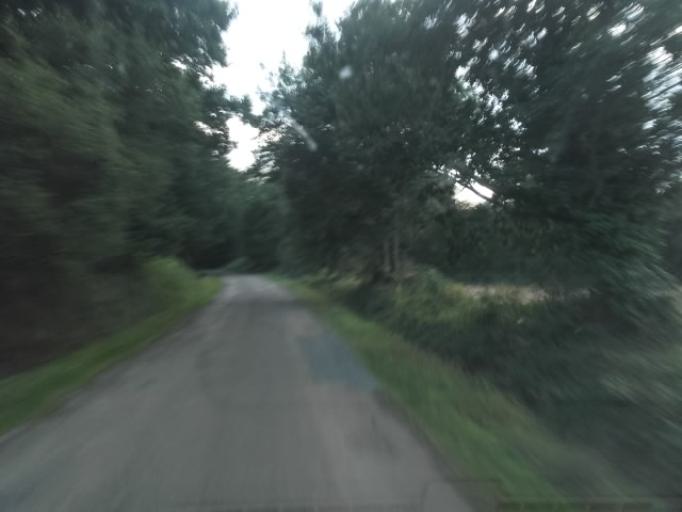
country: FR
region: Brittany
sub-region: Departement des Cotes-d'Armor
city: Lanvollon
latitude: 48.6289
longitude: -2.9670
